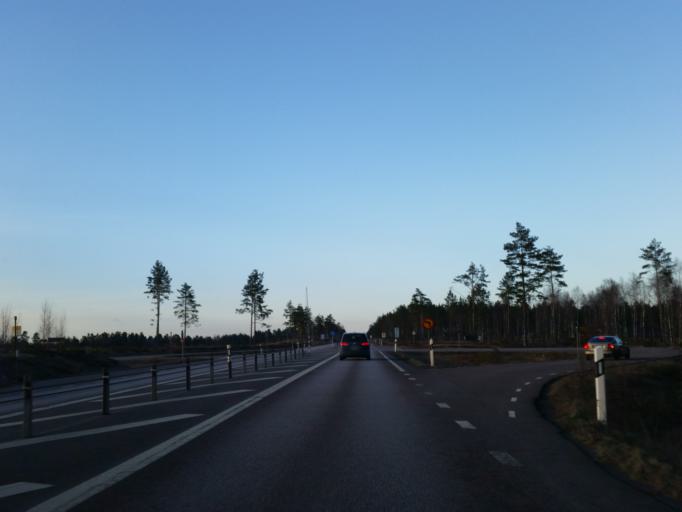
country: SE
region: Kalmar
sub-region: Oskarshamns Kommun
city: Oskarshamn
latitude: 57.3981
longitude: 16.4790
